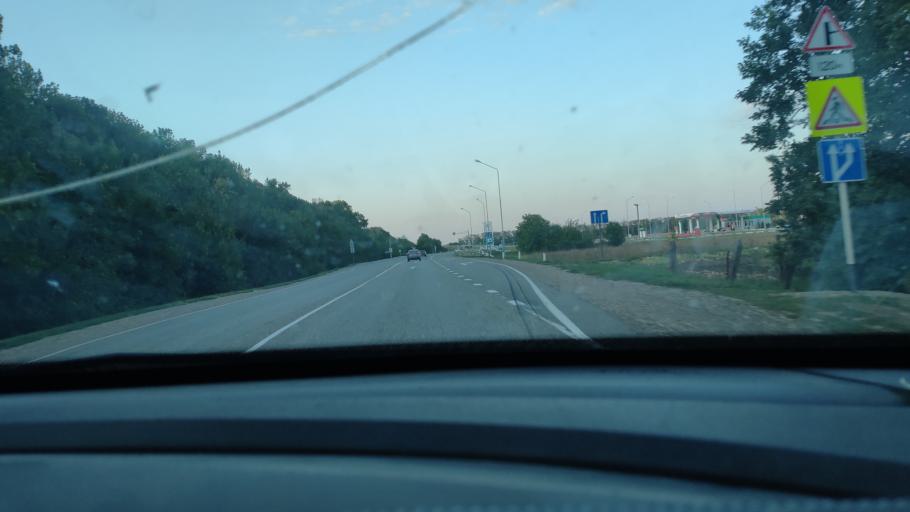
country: RU
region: Krasnodarskiy
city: Novominskaya
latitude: 46.4106
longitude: 39.0040
